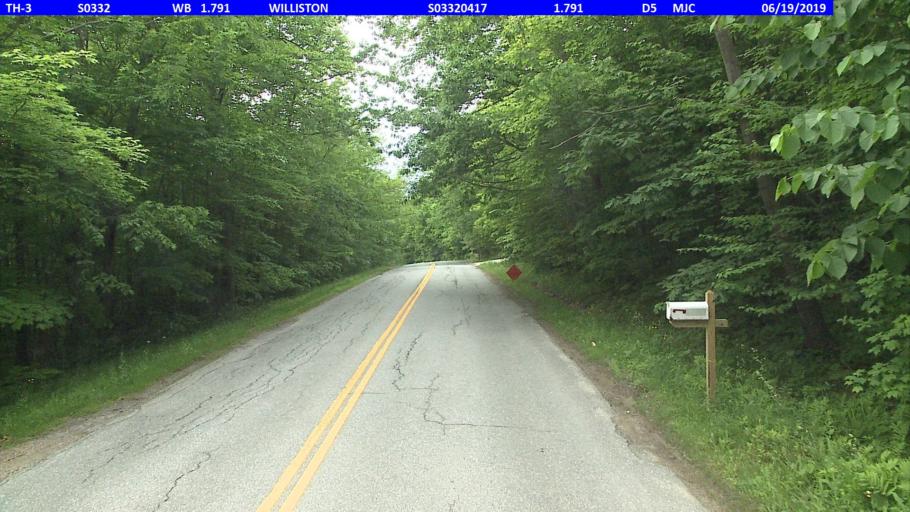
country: US
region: Vermont
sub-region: Chittenden County
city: Williston
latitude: 44.4186
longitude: -73.0895
